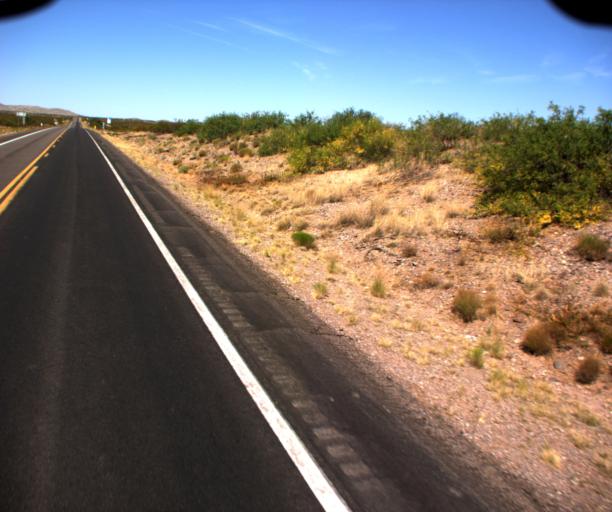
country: US
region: Arizona
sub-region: Greenlee County
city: Clifton
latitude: 32.7385
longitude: -109.1420
